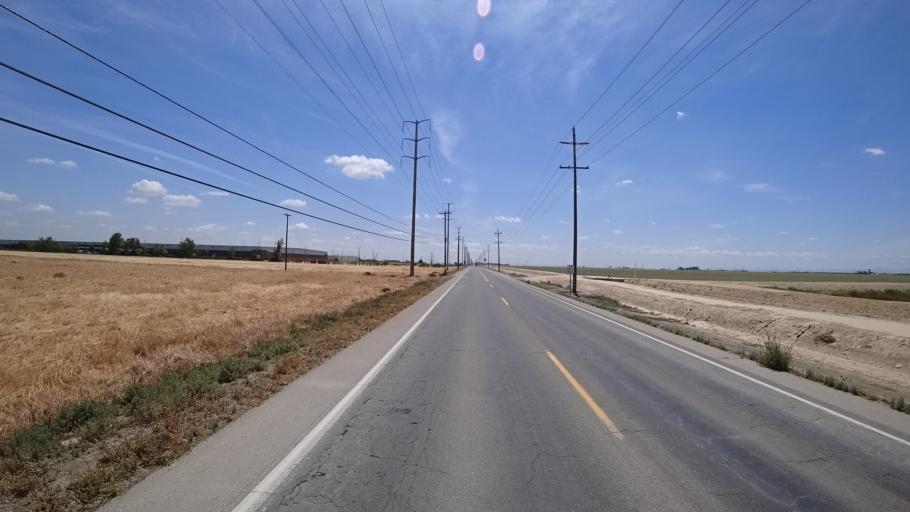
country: US
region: California
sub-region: Kings County
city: Home Garden
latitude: 36.2625
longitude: -119.6549
